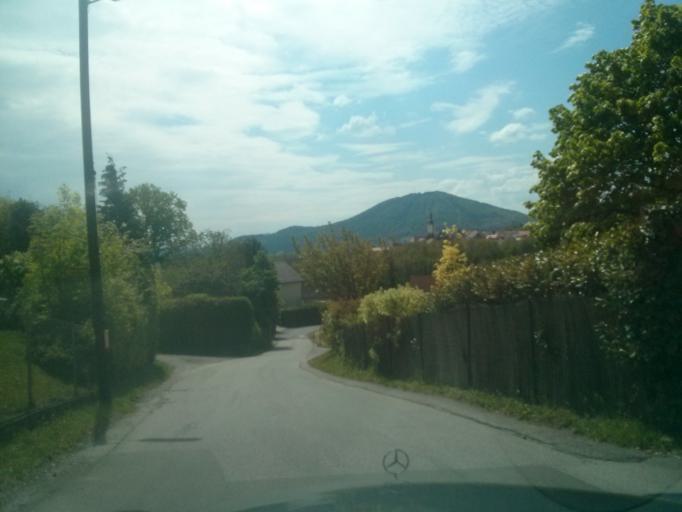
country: AT
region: Styria
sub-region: Politischer Bezirk Graz-Umgebung
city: Stattegg
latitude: 47.1221
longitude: 15.4174
